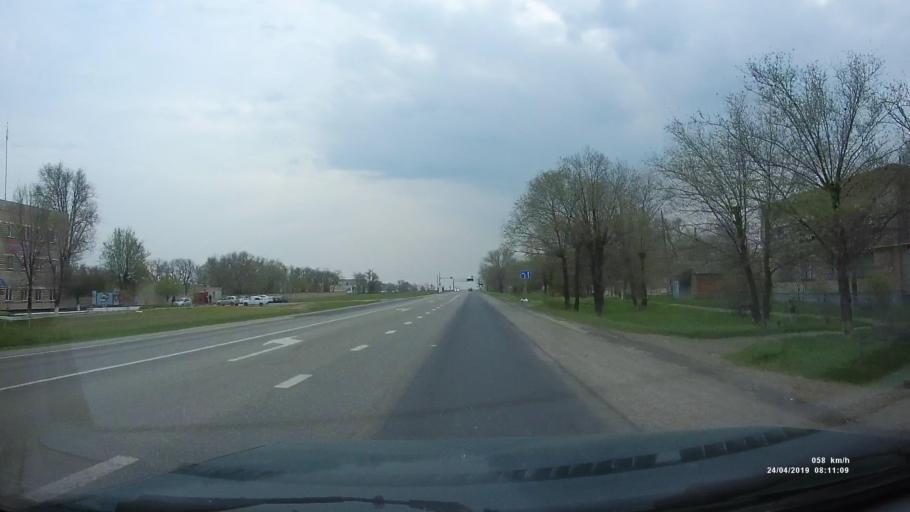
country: RU
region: Kalmykiya
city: Priyutnoye
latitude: 46.1010
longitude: 43.5248
